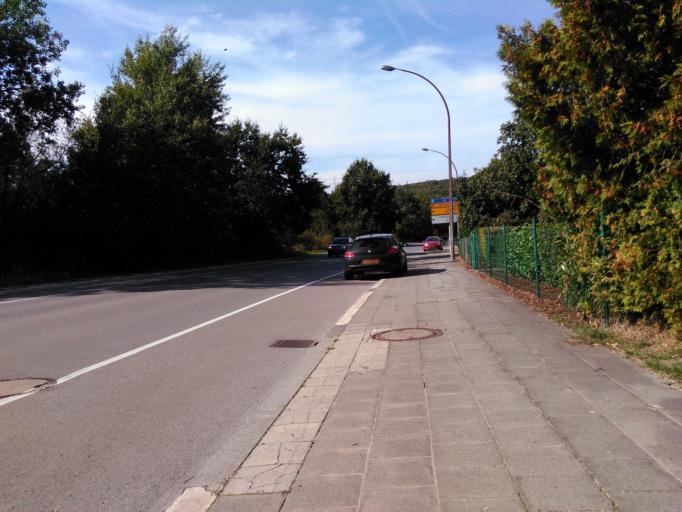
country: LU
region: Luxembourg
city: Belvaux
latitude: 49.5207
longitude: 5.9249
